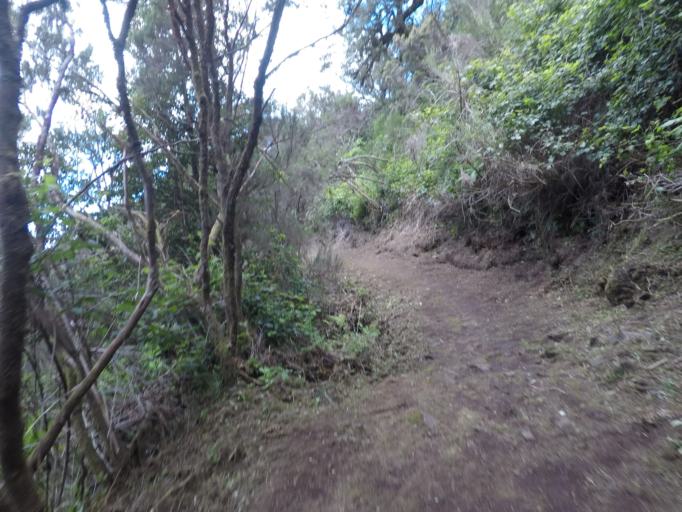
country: PT
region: Madeira
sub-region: Camara de Lobos
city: Curral das Freiras
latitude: 32.7585
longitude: -16.9735
